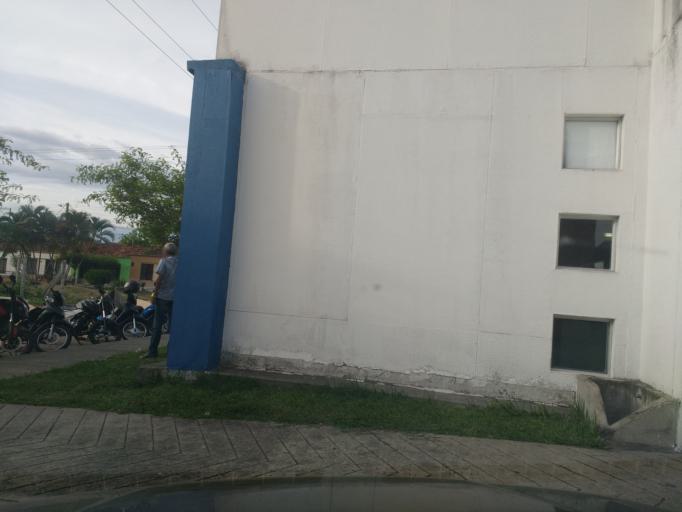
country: CO
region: Valle del Cauca
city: Cartago
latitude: 4.7601
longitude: -75.9253
